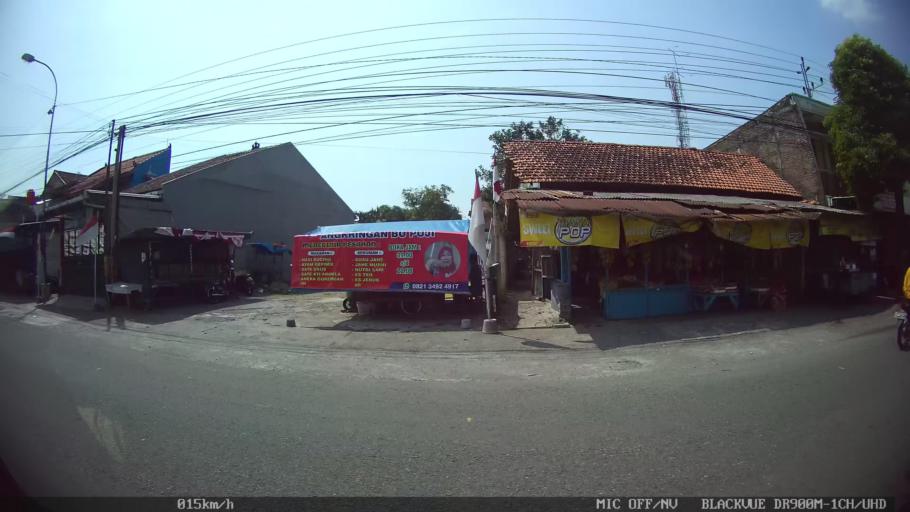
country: ID
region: Daerah Istimewa Yogyakarta
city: Yogyakarta
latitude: -7.8135
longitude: 110.3918
